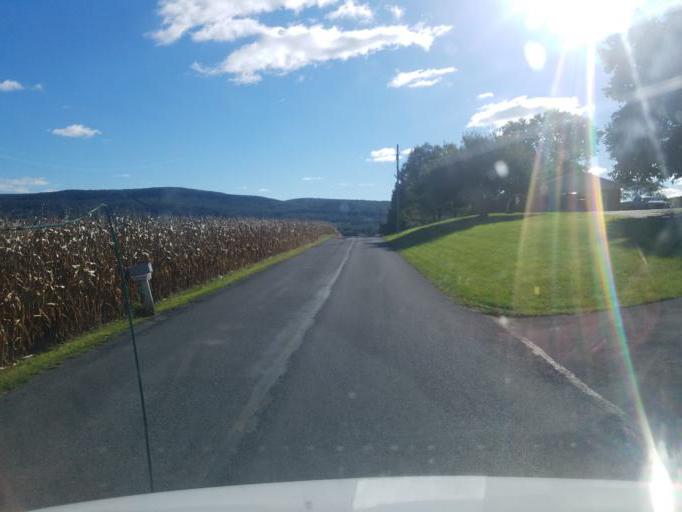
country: US
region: Pennsylvania
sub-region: Franklin County
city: Mont Alto
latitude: 39.8137
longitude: -77.5873
